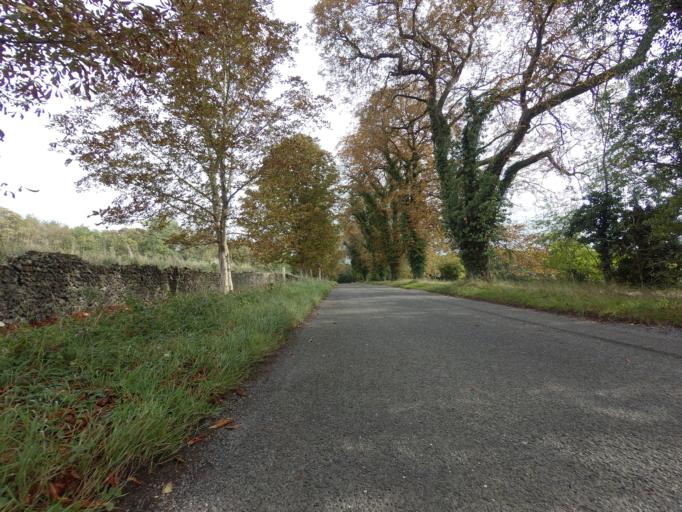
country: GB
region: England
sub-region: Essex
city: Saffron Walden
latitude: 52.0176
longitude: 0.2097
